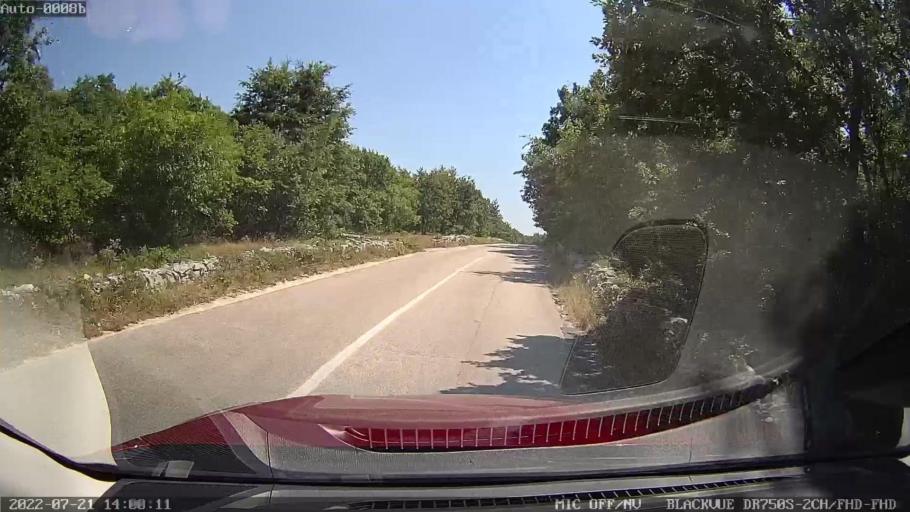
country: HR
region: Istarska
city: Vodnjan
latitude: 45.1001
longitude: 13.8680
